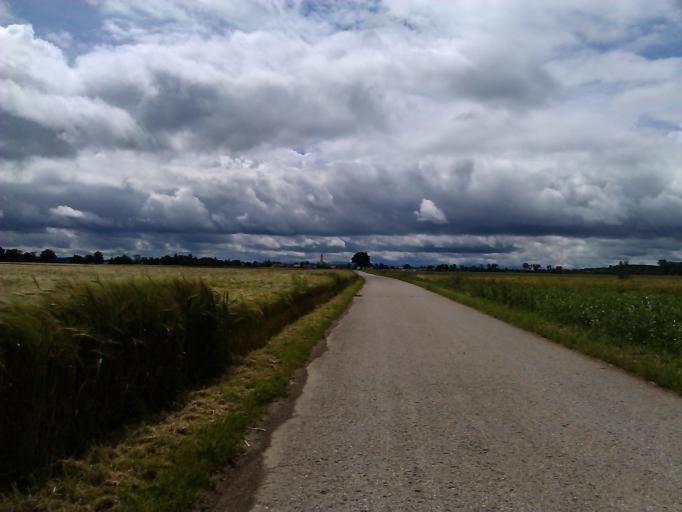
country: DE
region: Bavaria
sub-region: Swabia
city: Bad Worishofen
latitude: 47.9844
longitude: 10.6104
